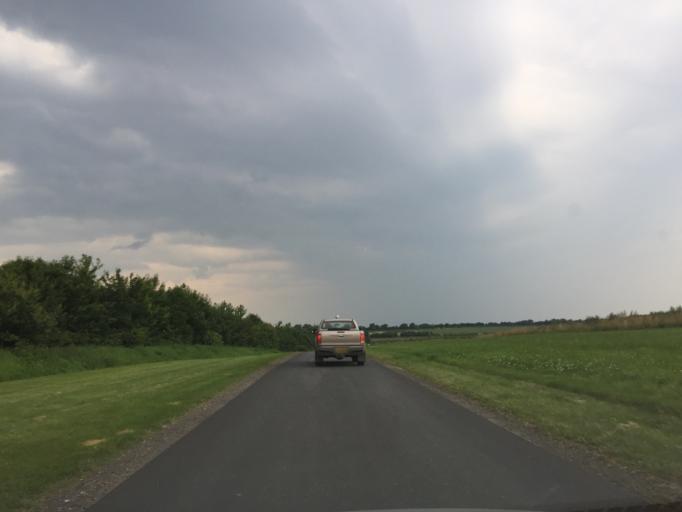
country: DK
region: Central Jutland
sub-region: Viborg Kommune
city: Bjerringbro
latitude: 56.3279
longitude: 9.6485
